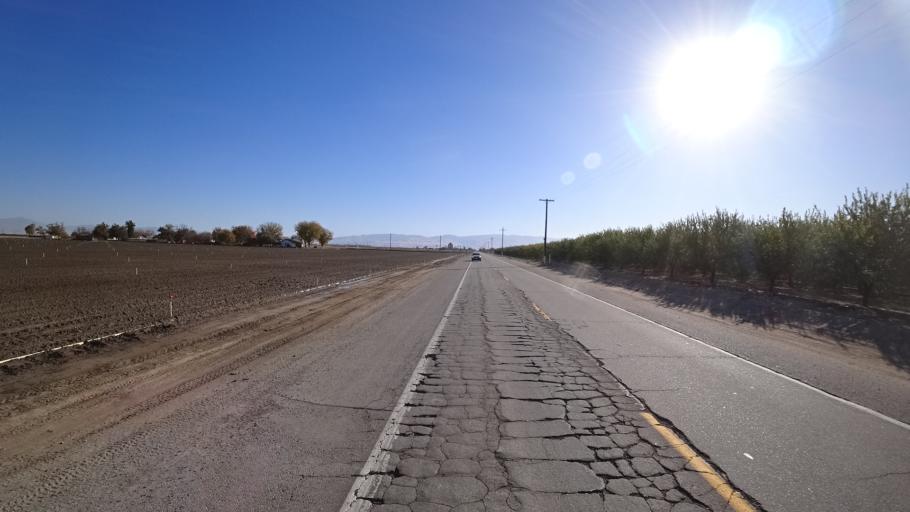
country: US
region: California
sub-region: Kern County
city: Greenacres
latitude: 35.2800
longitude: -119.1098
